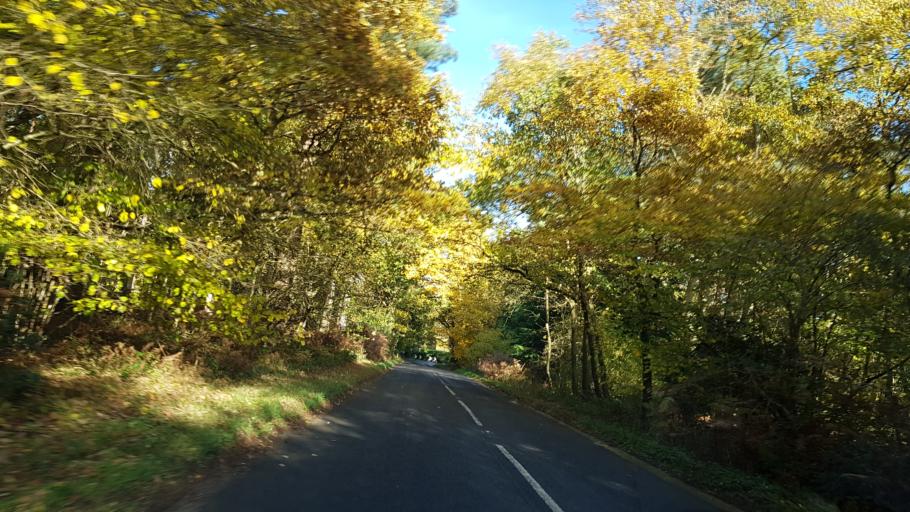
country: GB
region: England
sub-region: Surrey
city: Elstead
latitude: 51.1567
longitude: -0.7203
